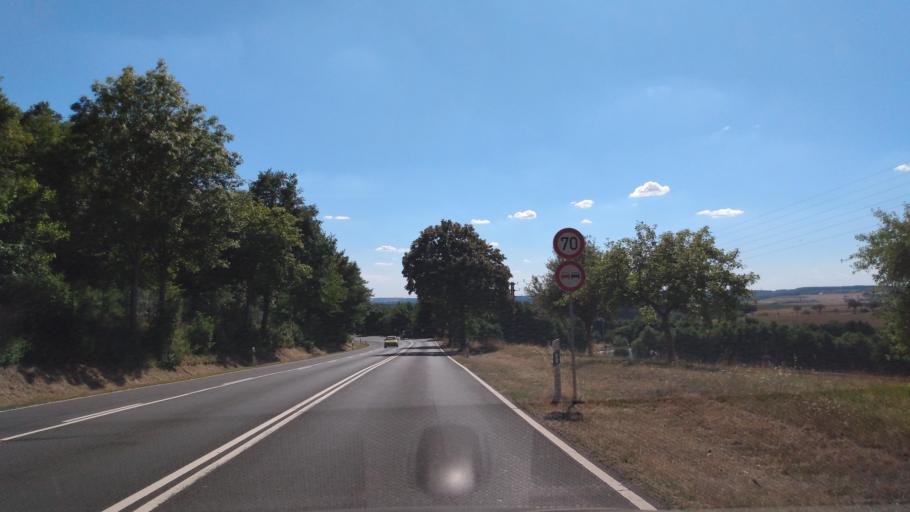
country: DE
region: Rheinland-Pfalz
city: Spangdahlem
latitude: 49.9764
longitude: 6.6828
